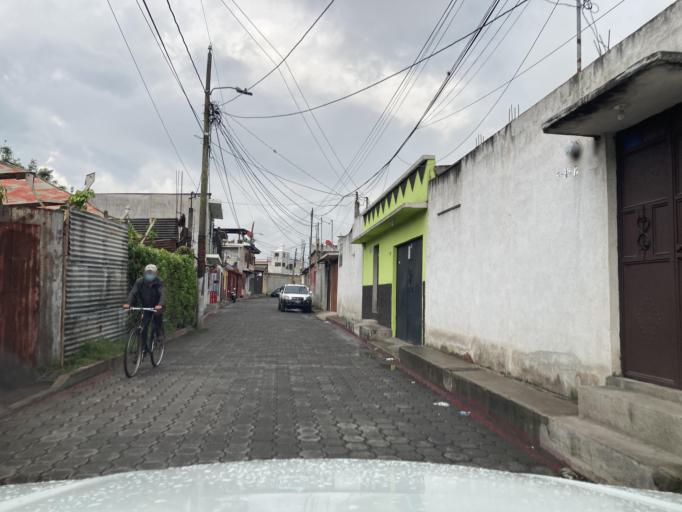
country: GT
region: Sacatepequez
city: San Miguel Duenas
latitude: 14.5232
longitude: -90.7948
